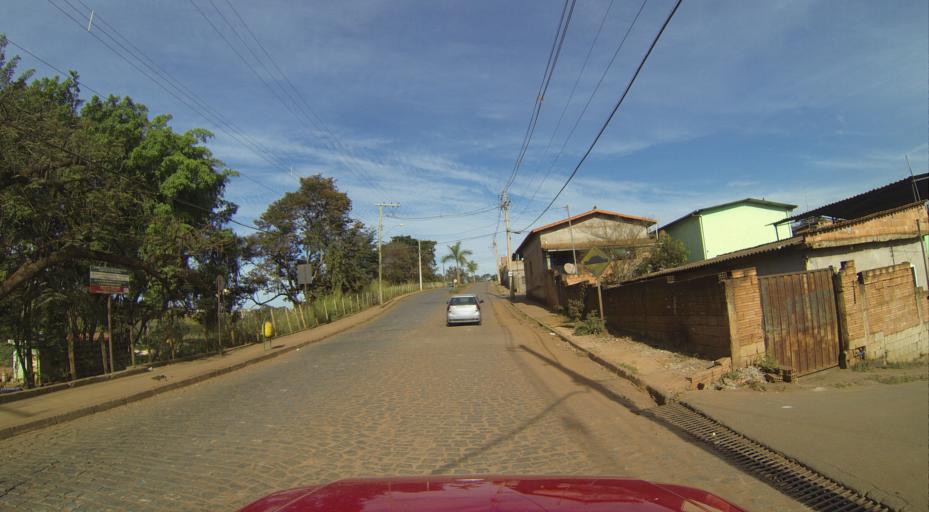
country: BR
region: Minas Gerais
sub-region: Brumadinho
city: Brumadinho
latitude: -20.1380
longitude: -44.2151
